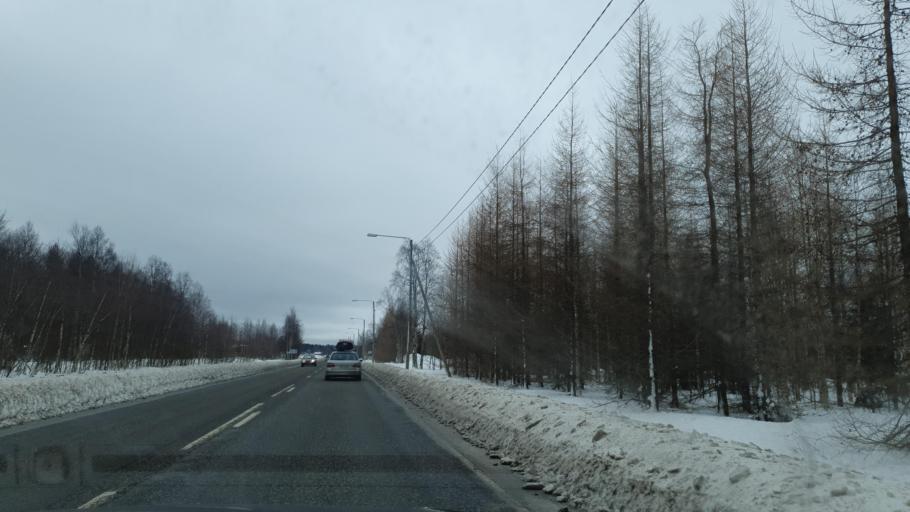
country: FI
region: Lapland
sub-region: Kemi-Tornio
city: Tornio
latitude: 66.0578
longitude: 23.9997
